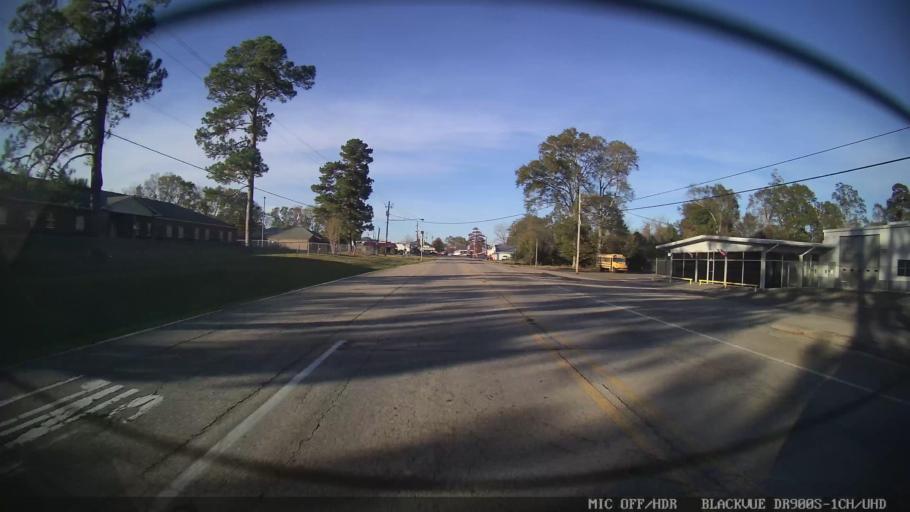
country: US
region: Mississippi
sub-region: Lamar County
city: Purvis
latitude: 31.1400
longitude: -89.4056
